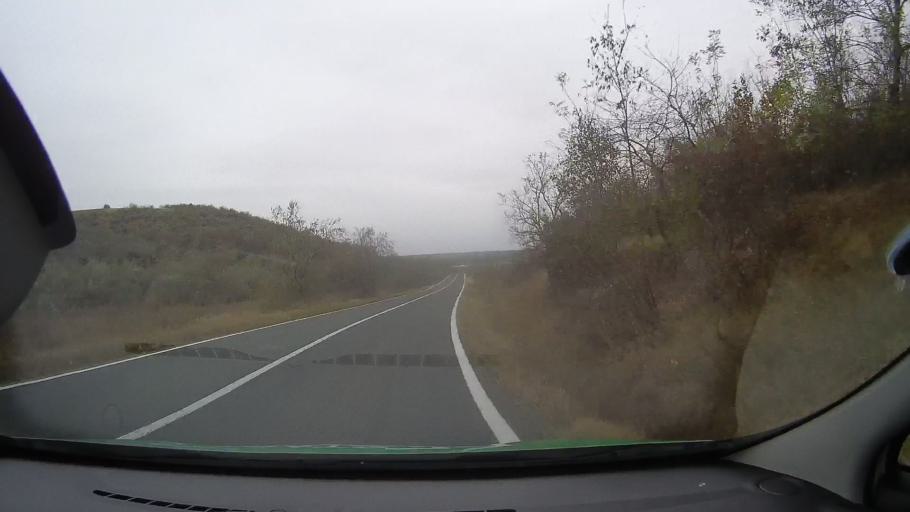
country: RO
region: Constanta
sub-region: Comuna Garliciu
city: Garliciu
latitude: 44.7065
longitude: 28.0693
